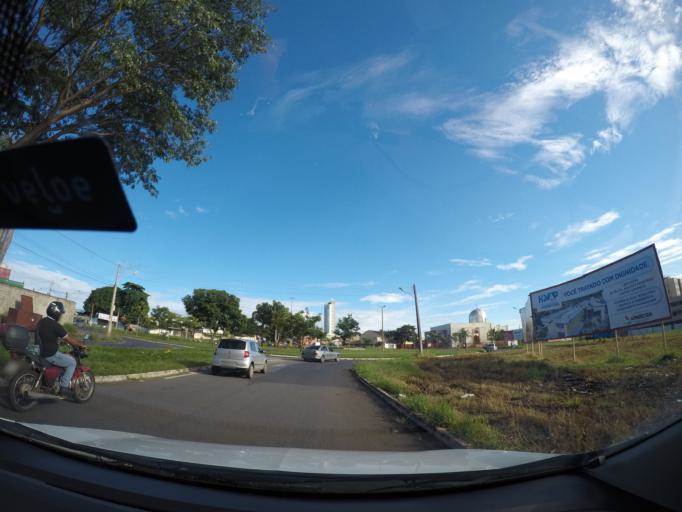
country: BR
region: Goias
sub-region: Goiania
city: Goiania
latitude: -16.7482
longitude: -49.2751
